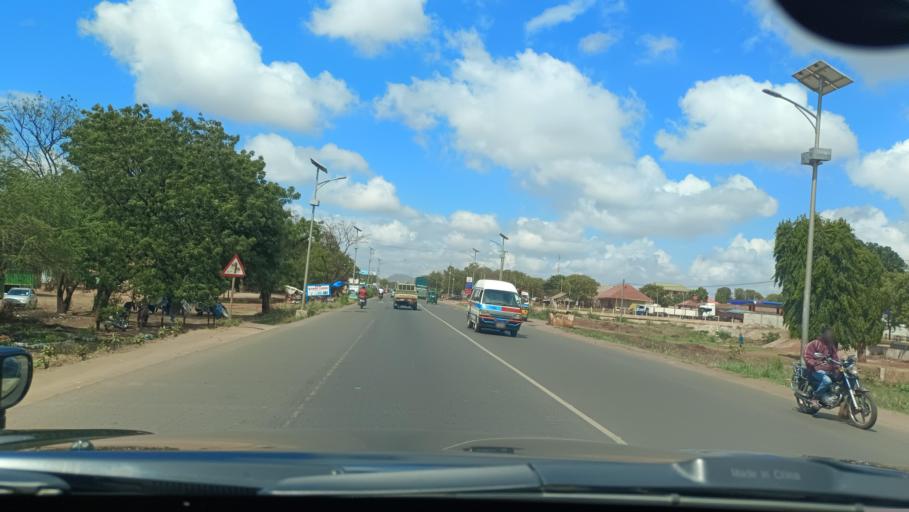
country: TZ
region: Morogoro
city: Morogoro
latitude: -6.8046
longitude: 37.6700
